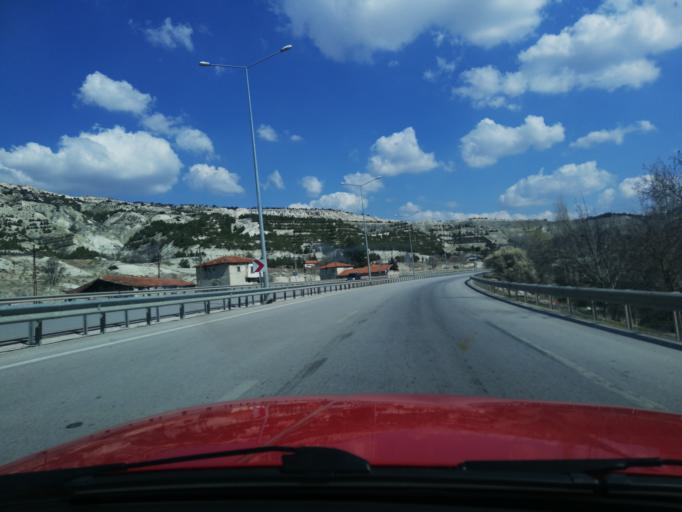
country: TR
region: Burdur
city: Burdur
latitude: 37.7089
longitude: 30.3022
